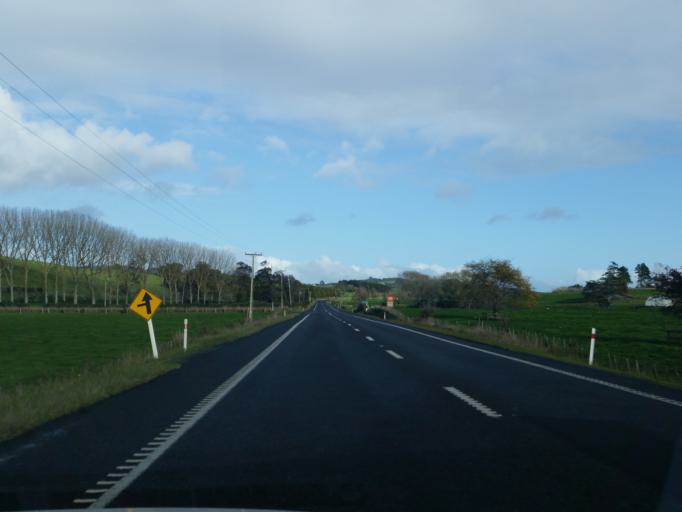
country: NZ
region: Waikato
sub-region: Hauraki District
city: Ngatea
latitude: -37.2864
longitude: 175.3919
